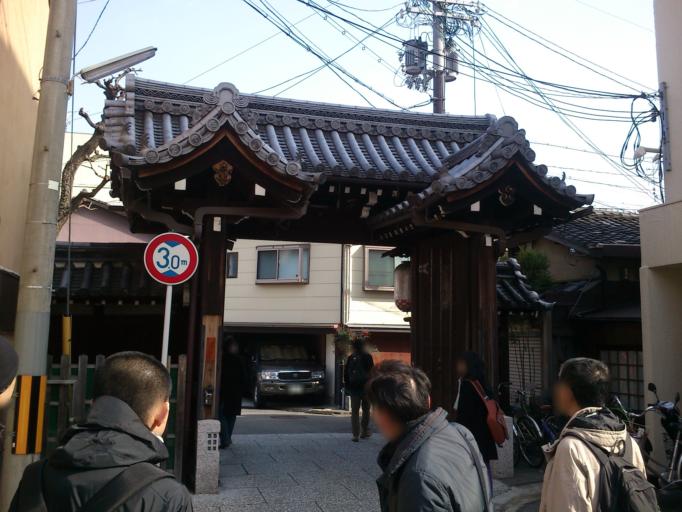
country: JP
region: Kyoto
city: Kyoto
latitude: 34.9927
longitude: 135.7447
